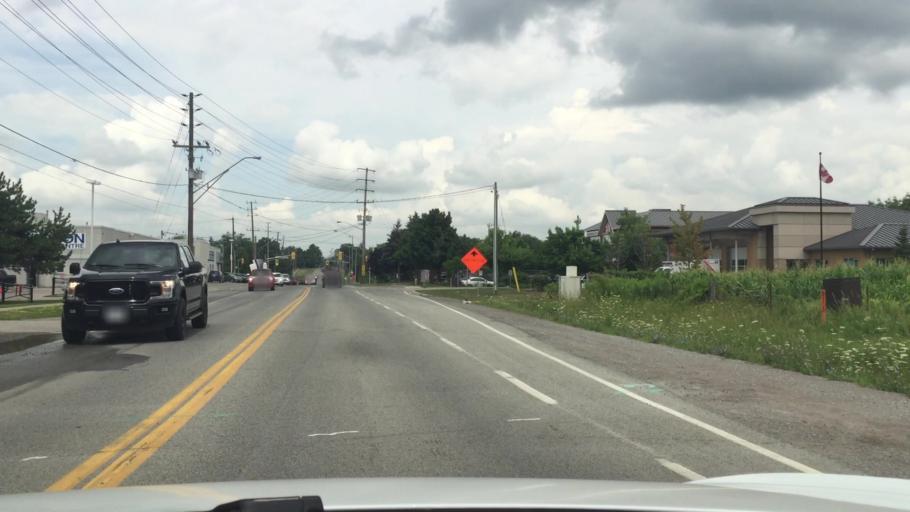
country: CA
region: Ontario
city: Oshawa
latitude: 43.9102
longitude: -78.7771
